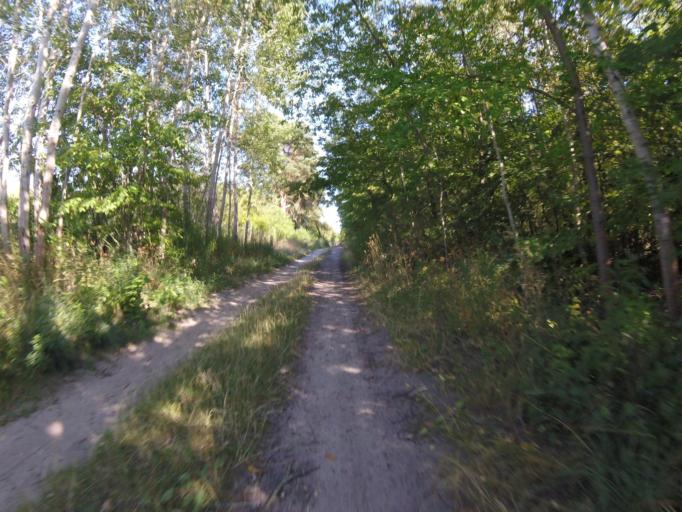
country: DE
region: Brandenburg
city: Konigs Wusterhausen
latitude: 52.3053
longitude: 13.6837
